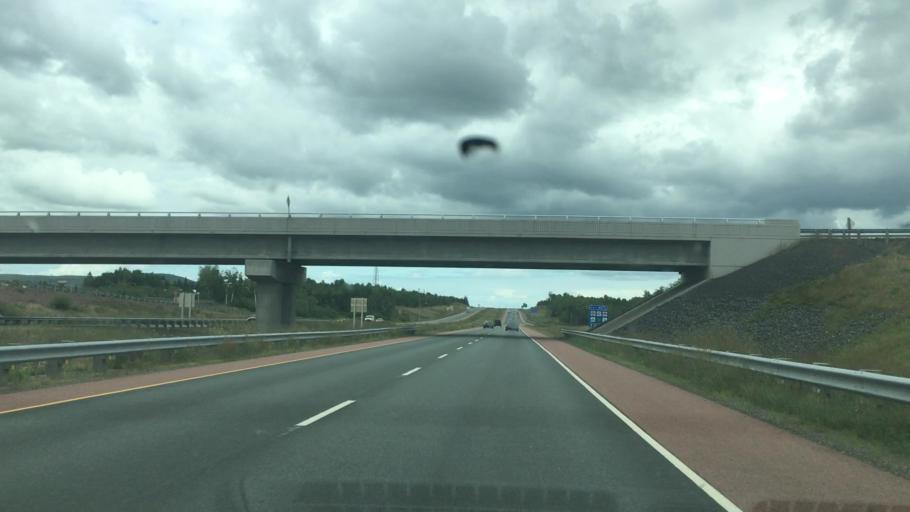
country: CA
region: Nova Scotia
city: Antigonish
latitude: 45.6004
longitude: -62.0243
